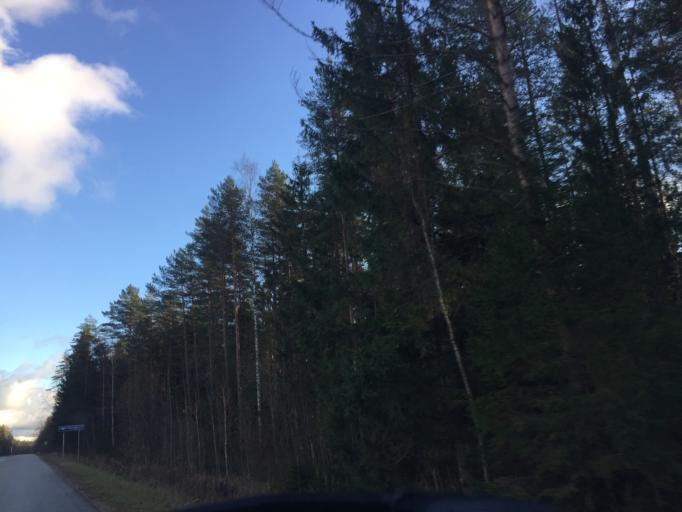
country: LV
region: Incukalns
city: Incukalns
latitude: 57.0883
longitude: 24.7608
